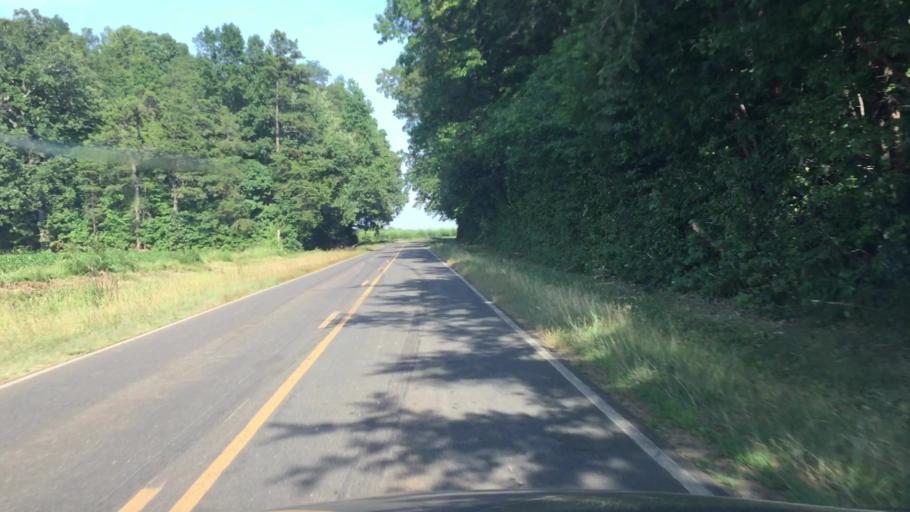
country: US
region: North Carolina
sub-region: Rockingham County
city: Reidsville
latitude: 36.2740
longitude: -79.5698
